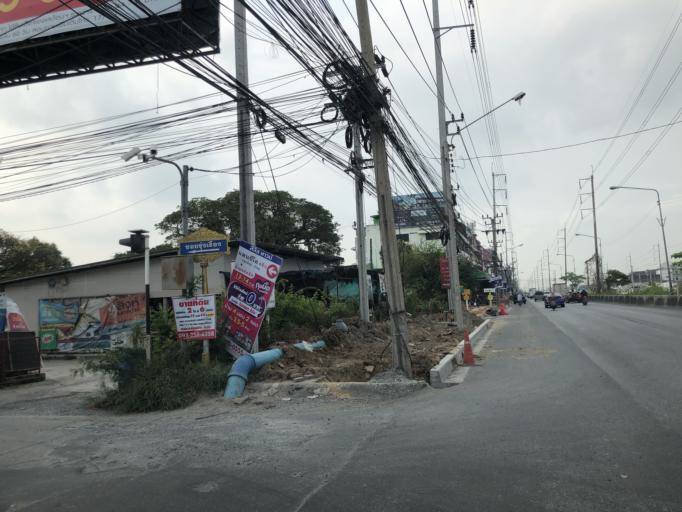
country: TH
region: Bangkok
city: Bang Na
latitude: 13.5866
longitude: 100.6981
